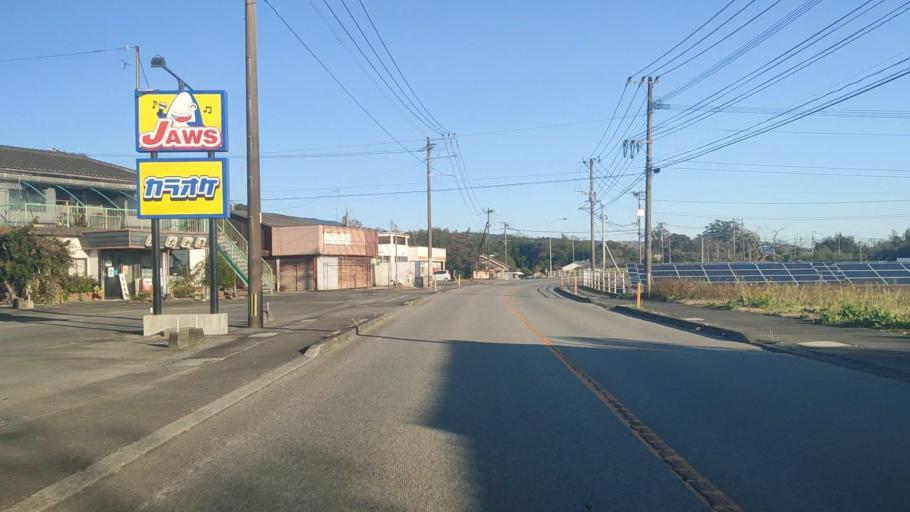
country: JP
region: Miyazaki
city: Takanabe
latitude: 32.2385
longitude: 131.5483
